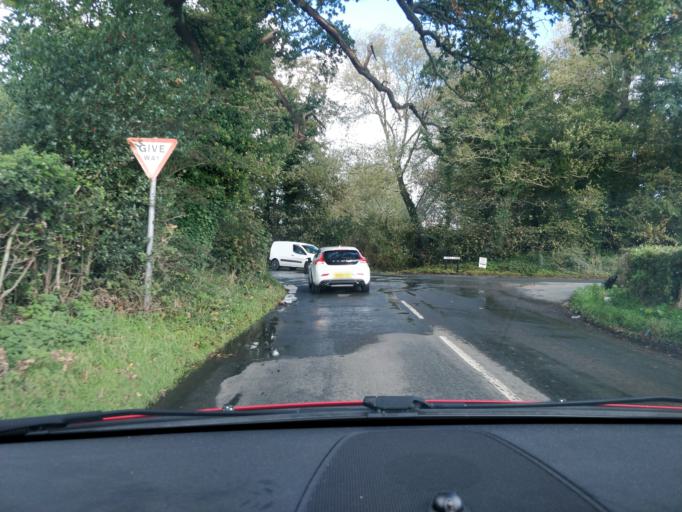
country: GB
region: England
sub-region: Lancashire
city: Parbold
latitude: 53.6127
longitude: -2.7824
